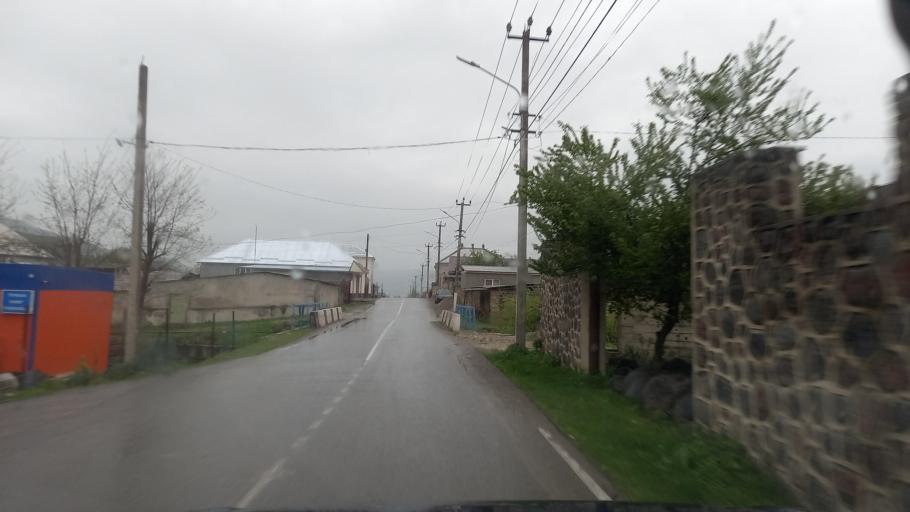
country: RU
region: Kabardino-Balkariya
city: Gundelen
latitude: 43.5952
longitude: 43.1747
